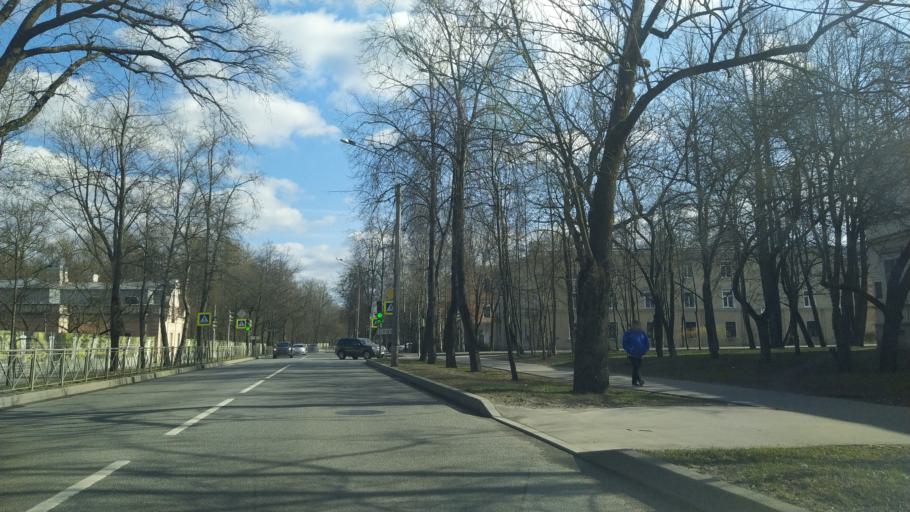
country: RU
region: St.-Petersburg
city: Pushkin
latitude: 59.7092
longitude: 30.4139
